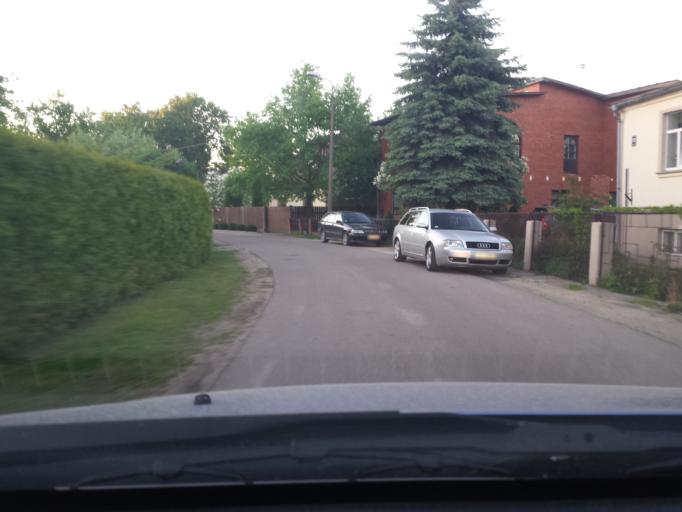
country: LV
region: Riga
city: Jaunciems
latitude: 56.9792
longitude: 24.1960
